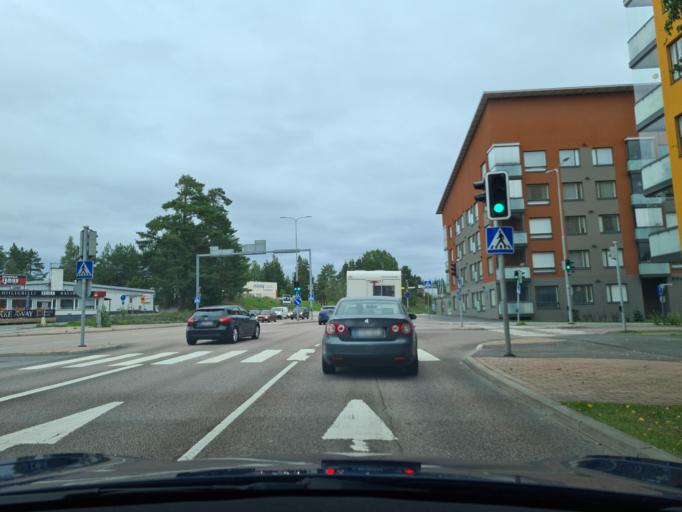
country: FI
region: South Karelia
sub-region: Lappeenranta
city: Lappeenranta
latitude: 61.0476
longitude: 28.1811
